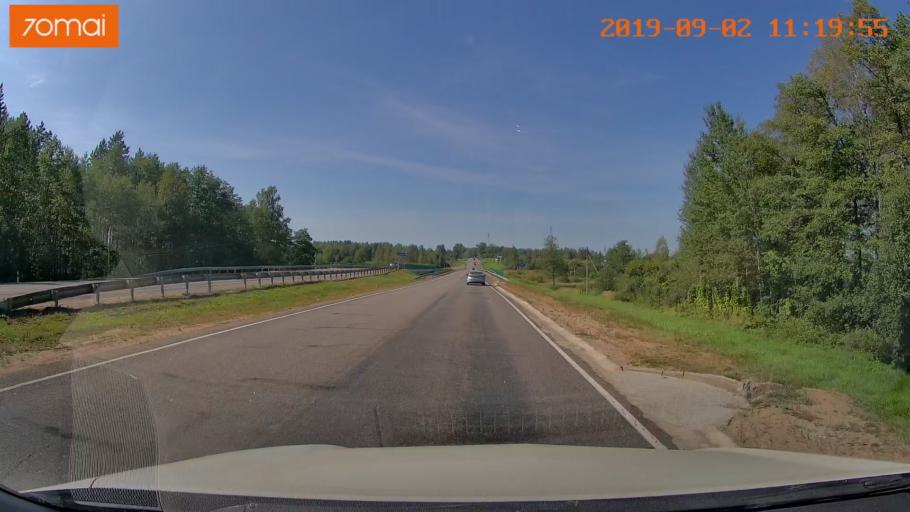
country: RU
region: Smolensk
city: Roslavl'
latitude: 54.0450
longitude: 33.0635
